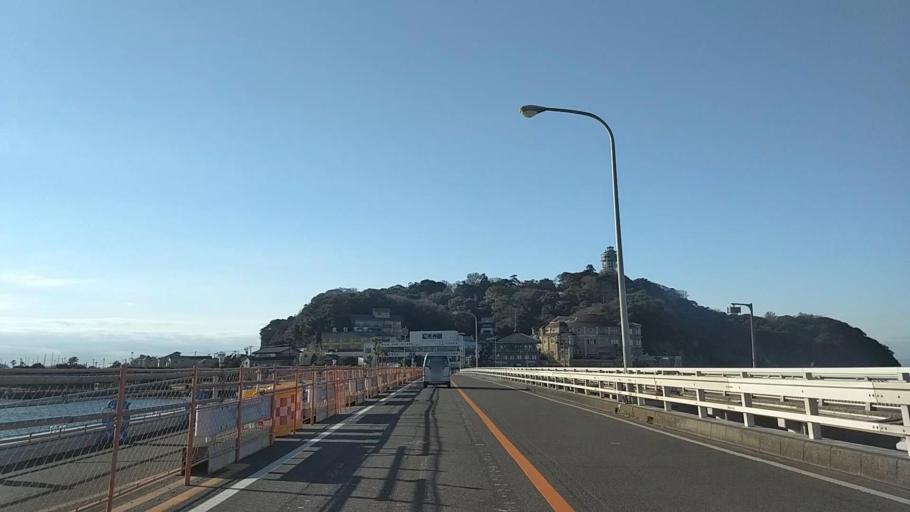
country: JP
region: Kanagawa
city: Fujisawa
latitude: 35.3044
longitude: 139.4823
